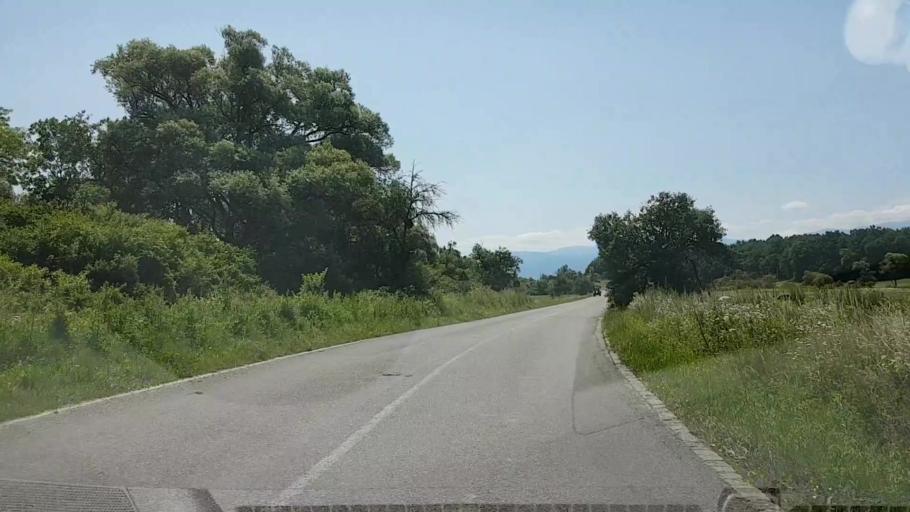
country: RO
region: Brasov
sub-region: Comuna Cincu
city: Cincu
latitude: 45.8769
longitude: 24.8182
